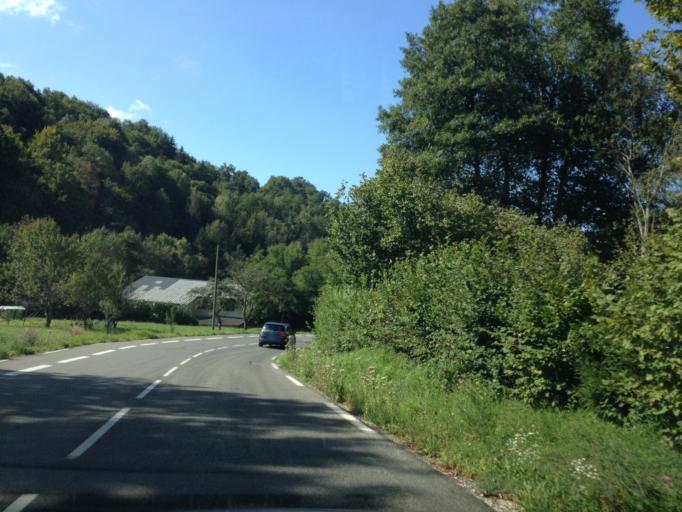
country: FR
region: Rhone-Alpes
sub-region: Departement de la Savoie
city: Gresy-sur-Aix
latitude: 45.7427
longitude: 5.9756
